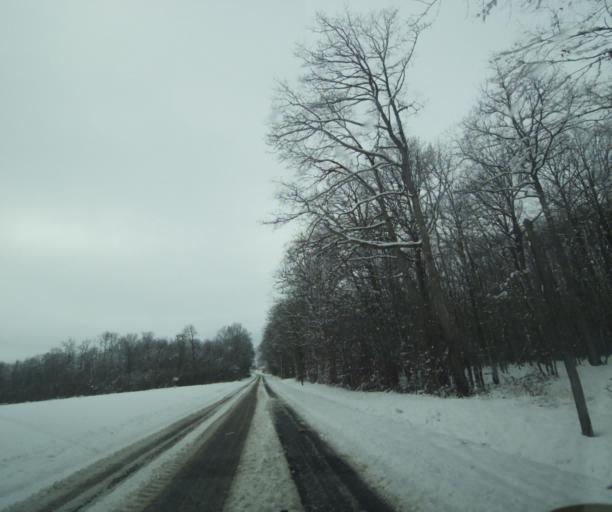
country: FR
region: Champagne-Ardenne
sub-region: Departement de la Haute-Marne
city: Montier-en-Der
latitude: 48.5294
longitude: 4.7340
